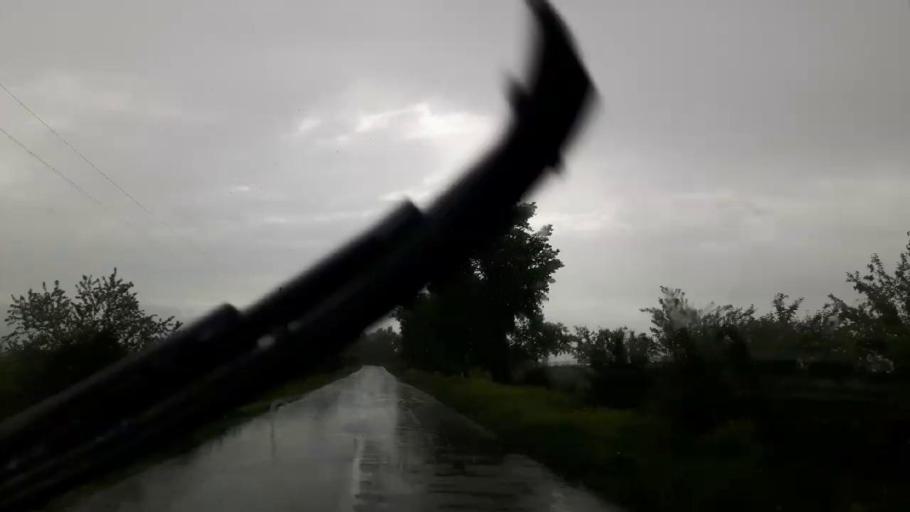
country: GE
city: Agara
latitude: 42.0129
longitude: 43.7929
